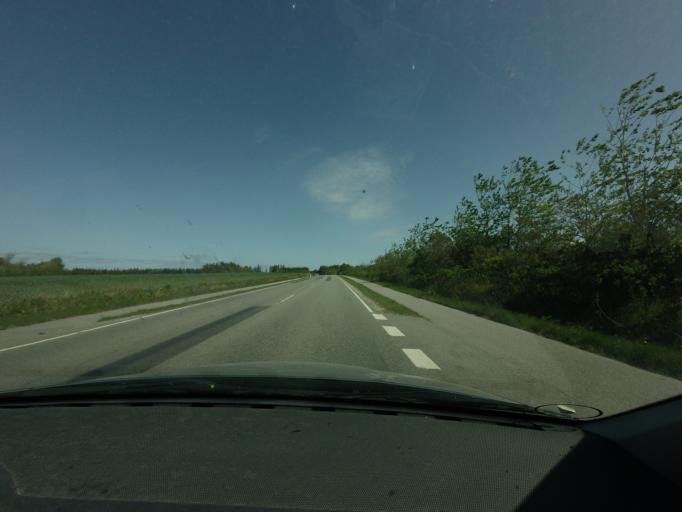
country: DK
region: North Denmark
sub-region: Jammerbugt Kommune
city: Pandrup
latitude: 57.3265
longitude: 9.7093
